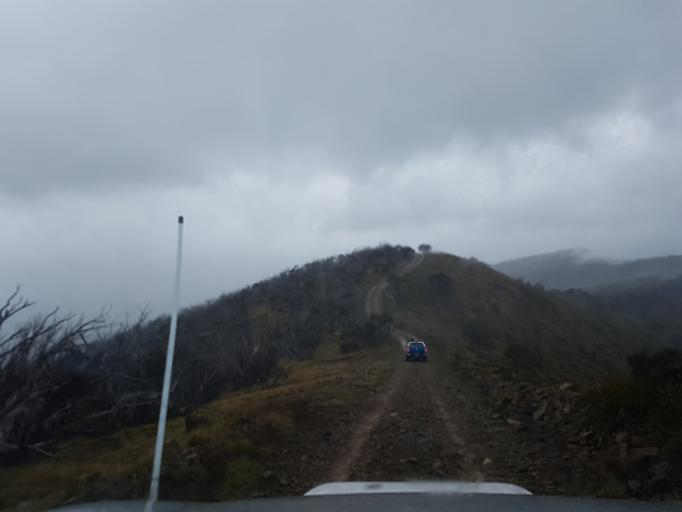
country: AU
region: Victoria
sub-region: Alpine
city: Mount Beauty
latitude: -37.0953
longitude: 147.0573
